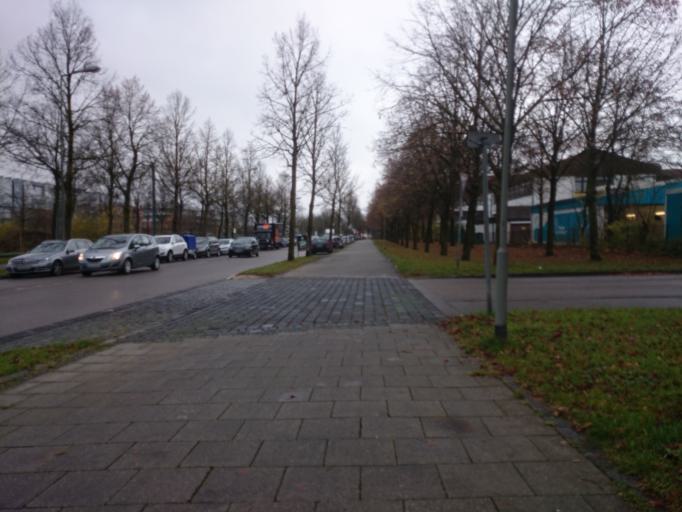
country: DE
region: Bavaria
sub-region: Swabia
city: Augsburg
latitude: 48.3289
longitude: 10.8993
